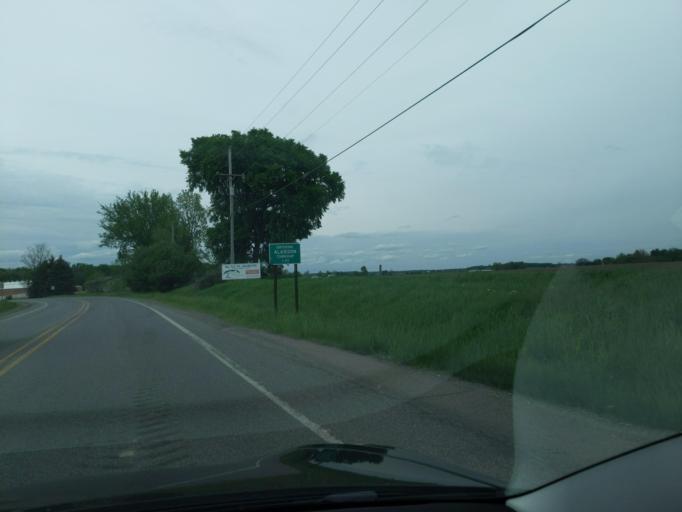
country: US
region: Michigan
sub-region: Ingham County
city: Mason
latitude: 42.5966
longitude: -84.4431
